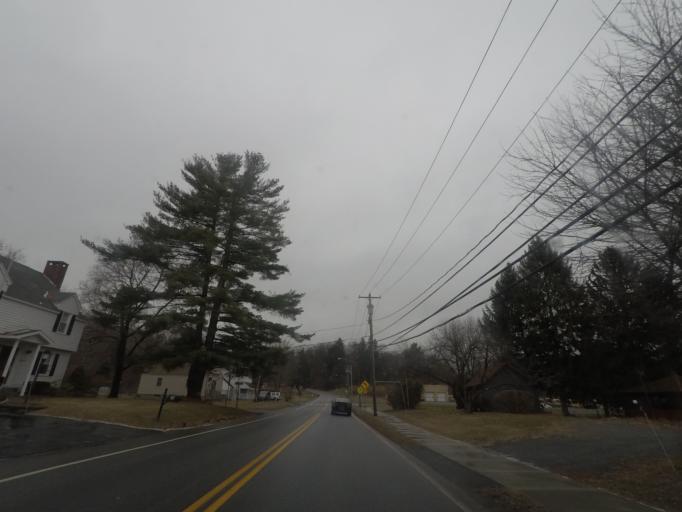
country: US
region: New York
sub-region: Saratoga County
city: Mechanicville
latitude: 42.9006
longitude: -73.6990
